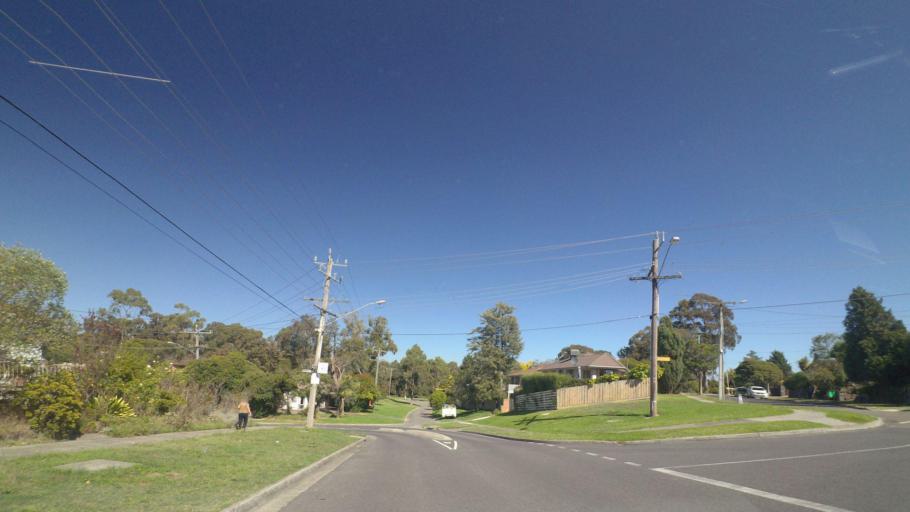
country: AU
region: Victoria
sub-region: Manningham
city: Donvale
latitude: -37.8008
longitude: 145.1689
